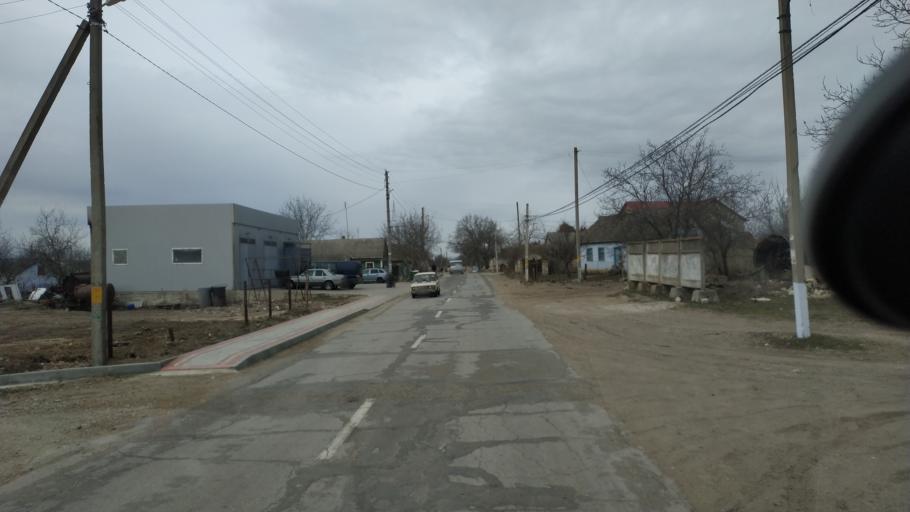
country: MD
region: Telenesti
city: Cocieri
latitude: 47.3130
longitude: 29.1059
